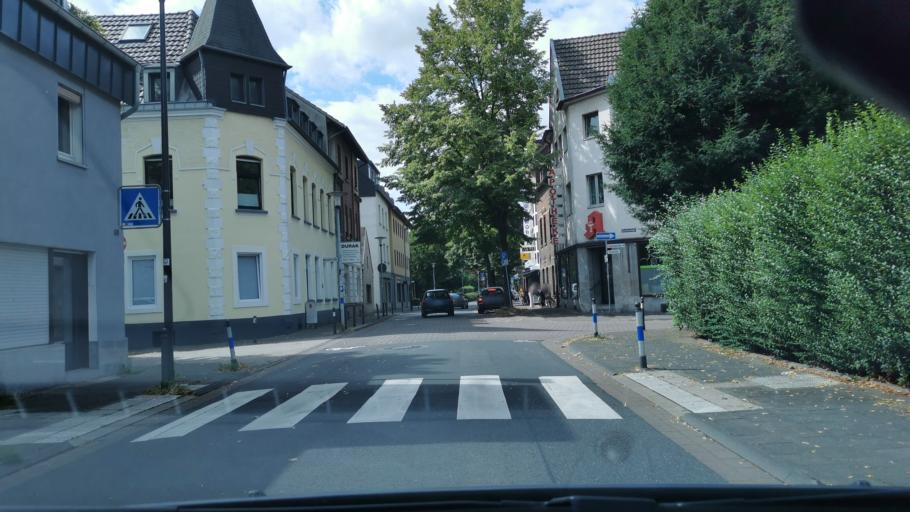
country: DE
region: North Rhine-Westphalia
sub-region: Regierungsbezirk Koln
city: Hurth
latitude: 50.8967
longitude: 6.8976
